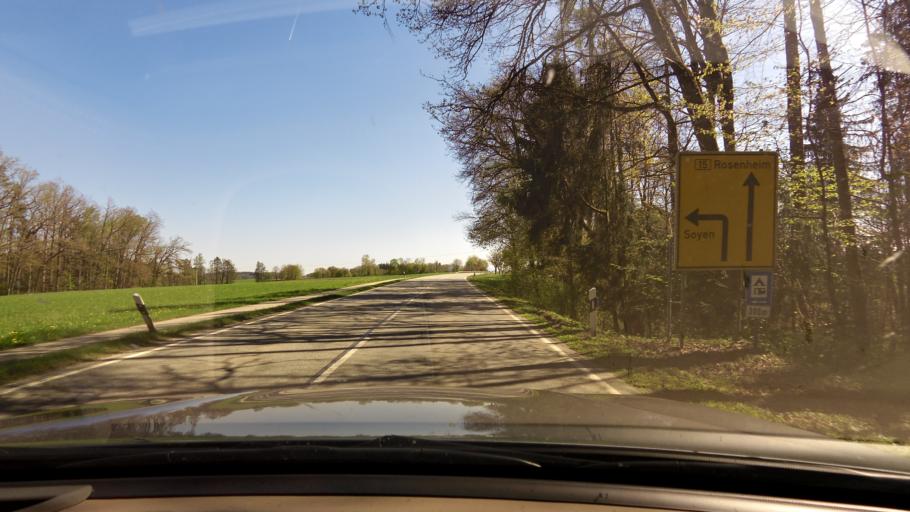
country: DE
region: Bavaria
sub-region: Upper Bavaria
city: Soyen
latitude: 48.1126
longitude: 12.1862
